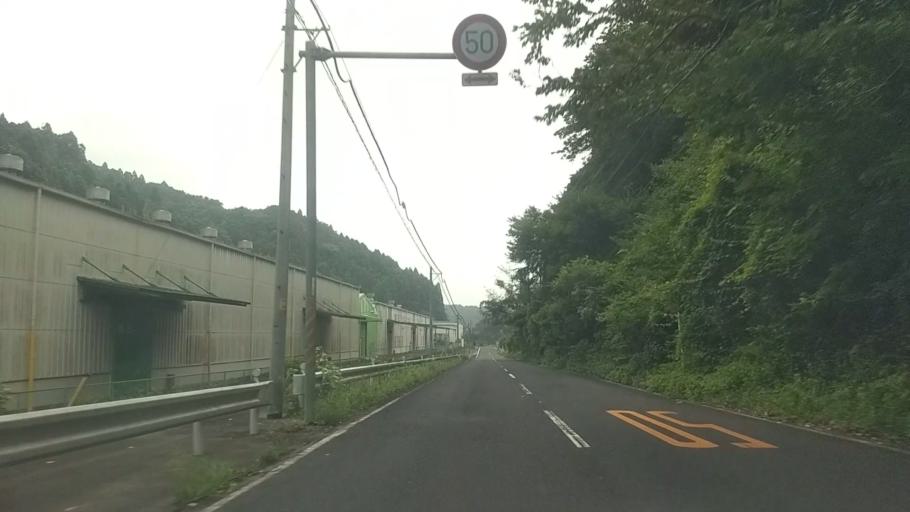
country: JP
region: Chiba
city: Katsuura
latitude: 35.2503
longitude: 140.2437
